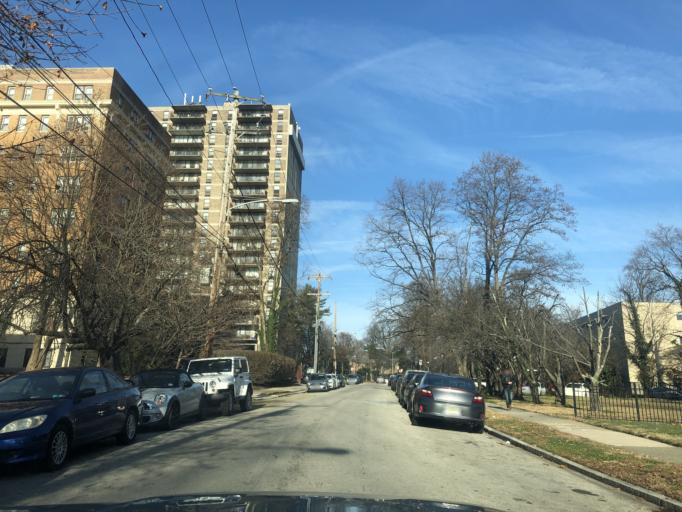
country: US
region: Pennsylvania
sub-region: Montgomery County
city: Bala-Cynwyd
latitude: 39.9899
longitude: -75.2470
